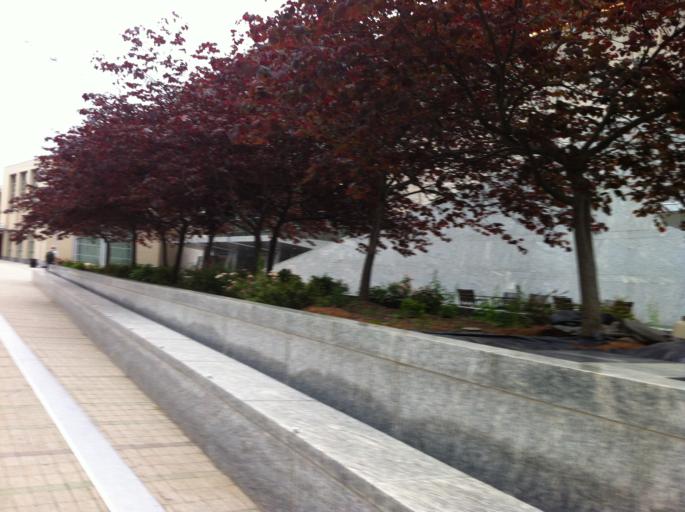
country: US
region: North Carolina
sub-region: Wake County
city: Raleigh
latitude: 35.7740
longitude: -78.6405
